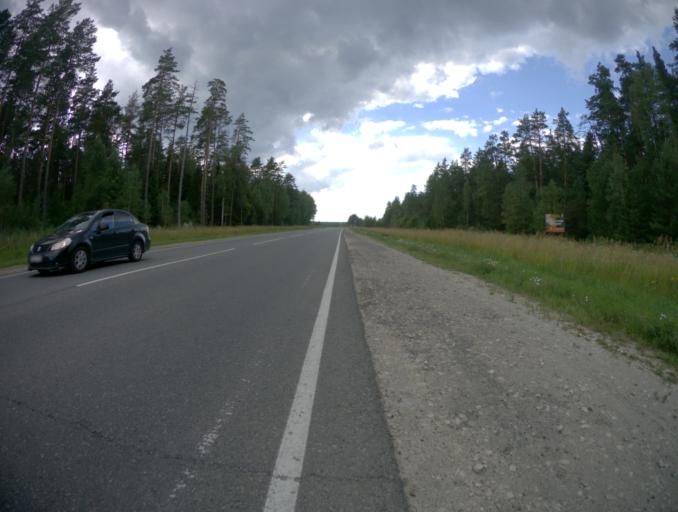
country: RU
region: Vladimir
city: Andreyevo
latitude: 55.9334
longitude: 41.1039
